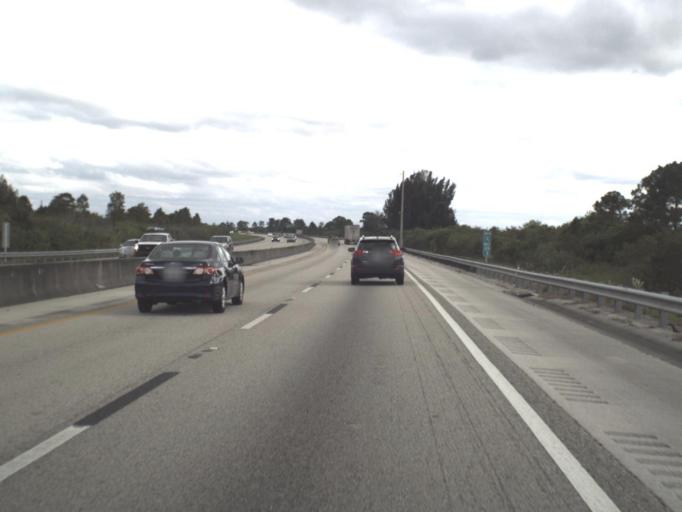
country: US
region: Florida
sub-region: Martin County
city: Hobe Sound
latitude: 27.0314
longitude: -80.2365
